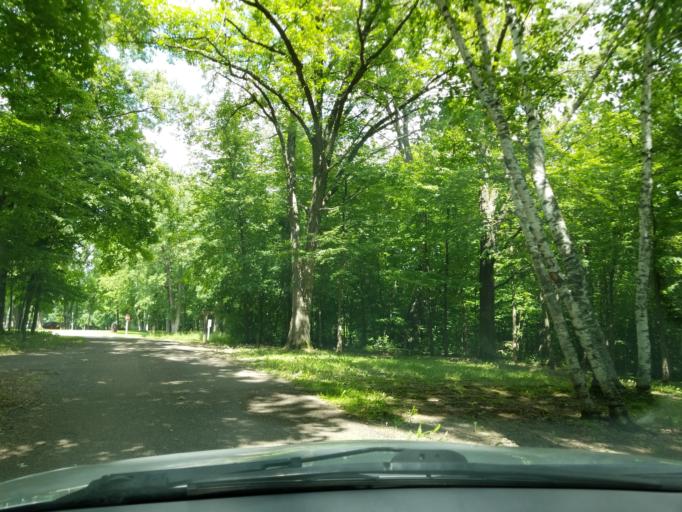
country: US
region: Wisconsin
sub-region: Saint Croix County
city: Glenwood City
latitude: 45.0031
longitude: -92.1720
